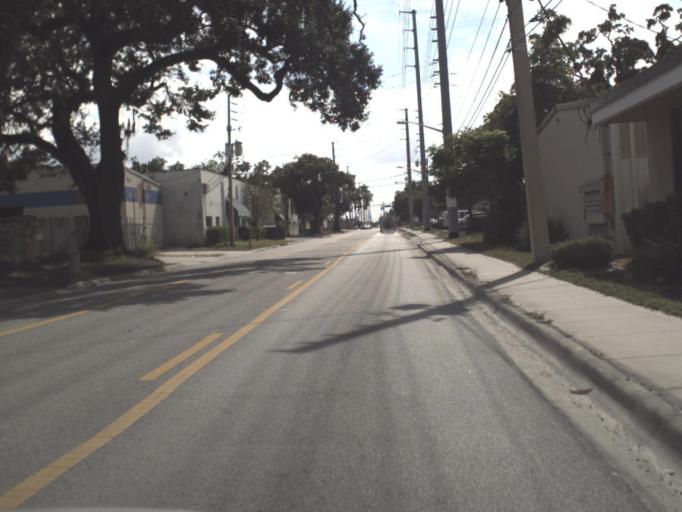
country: US
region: Florida
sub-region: Orange County
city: Orlando
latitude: 28.5227
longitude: -81.3847
